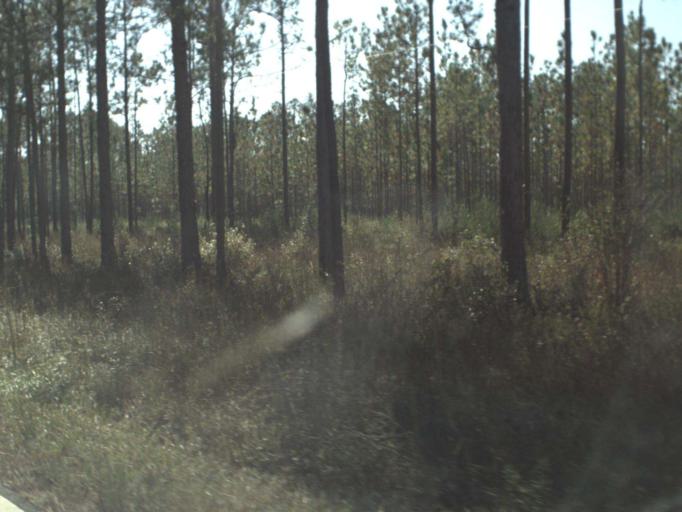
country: US
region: Florida
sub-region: Gulf County
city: Wewahitchka
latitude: 30.0671
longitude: -84.9834
